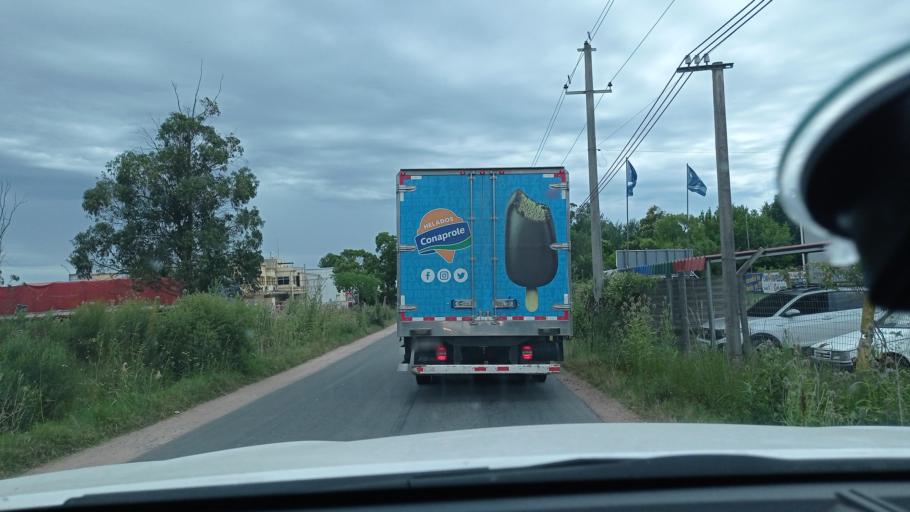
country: UY
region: Canelones
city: La Paz
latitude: -34.8085
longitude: -56.1899
